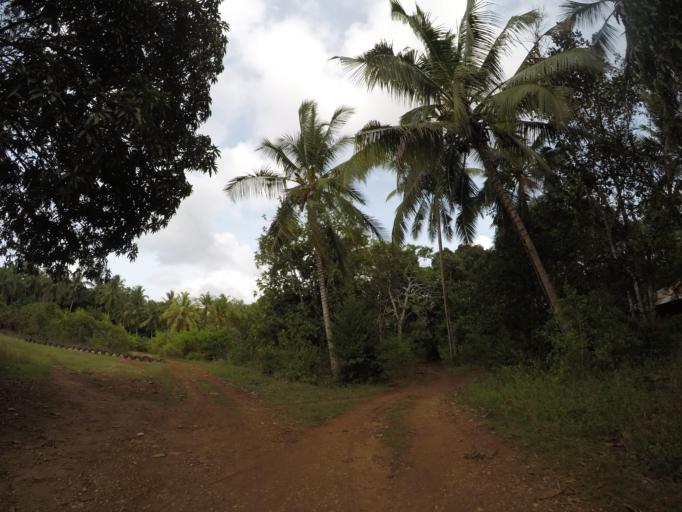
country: TZ
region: Zanzibar Central/South
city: Koani
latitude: -6.2154
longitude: 39.3223
